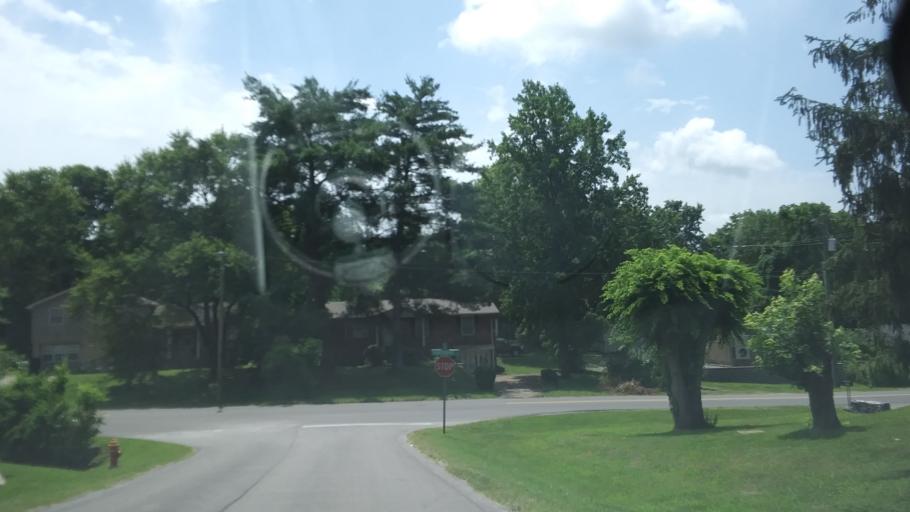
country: US
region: Tennessee
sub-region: Davidson County
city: Belle Meade
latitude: 36.1448
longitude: -86.8833
